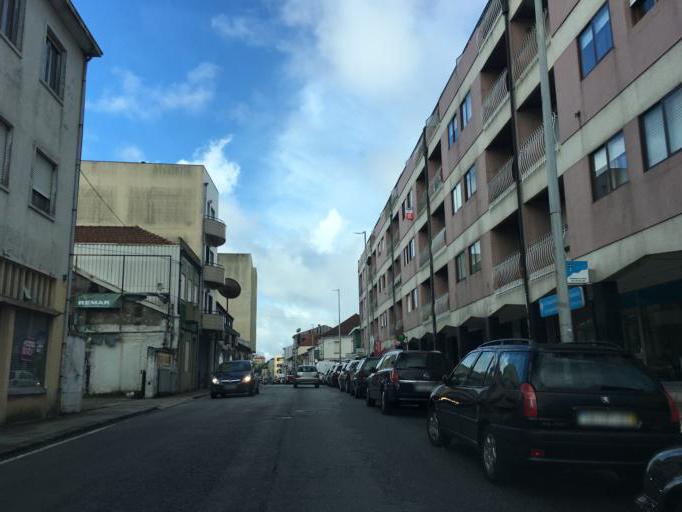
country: PT
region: Porto
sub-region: Matosinhos
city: Sao Mamede de Infesta
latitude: 41.1868
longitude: -8.6128
